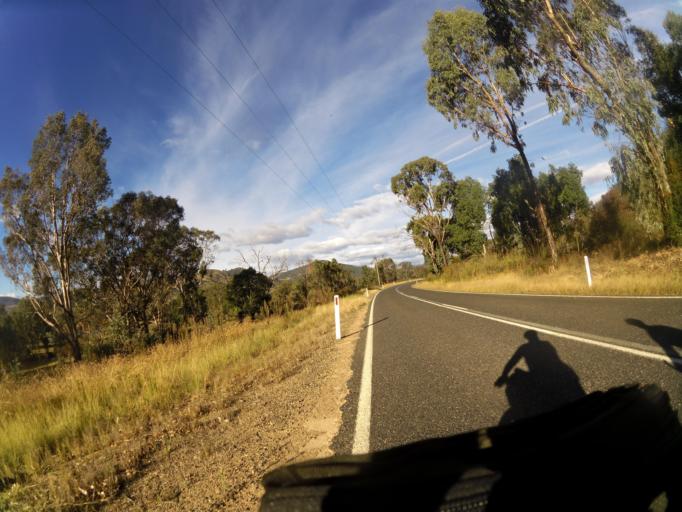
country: AU
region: New South Wales
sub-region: Greater Hume Shire
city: Holbrook
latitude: -35.9914
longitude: 147.8539
